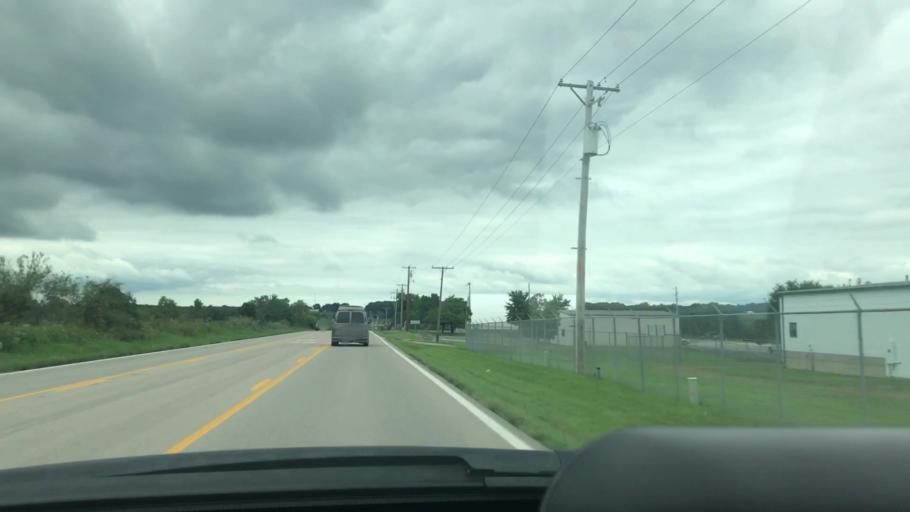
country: US
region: Missouri
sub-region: Dallas County
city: Buffalo
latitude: 37.6588
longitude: -93.1036
